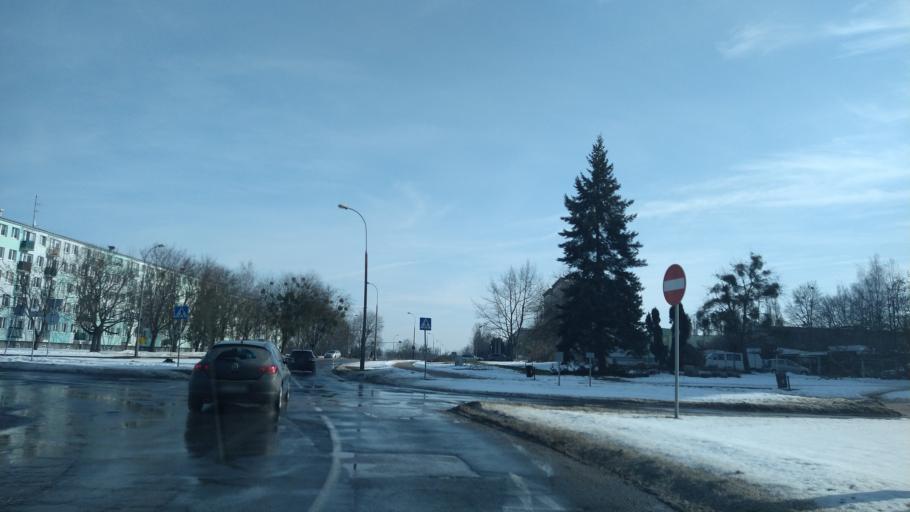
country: PL
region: Warmian-Masurian Voivodeship
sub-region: Powiat olsztynski
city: Olsztyn
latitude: 53.7727
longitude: 20.5006
